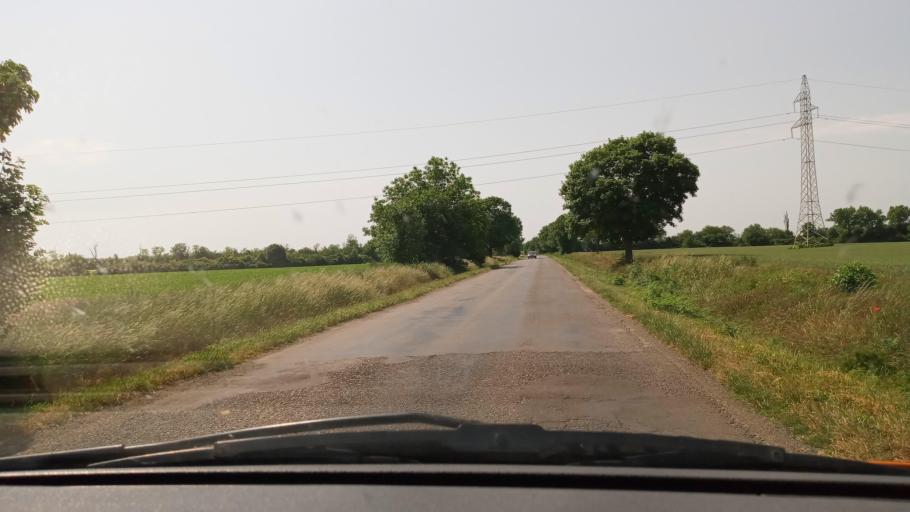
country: HU
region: Baranya
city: Szentlorinc
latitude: 46.0286
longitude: 18.0316
